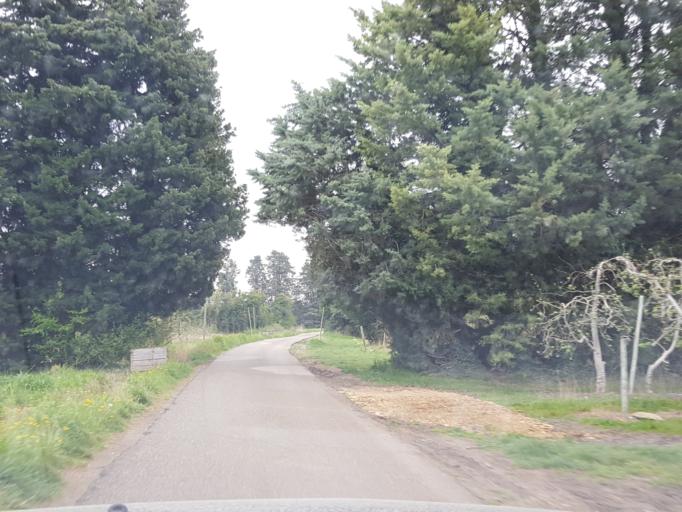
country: FR
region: Provence-Alpes-Cote d'Azur
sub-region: Departement du Vaucluse
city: Saint-Saturnin-les-Avignon
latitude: 43.9779
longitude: 4.9297
